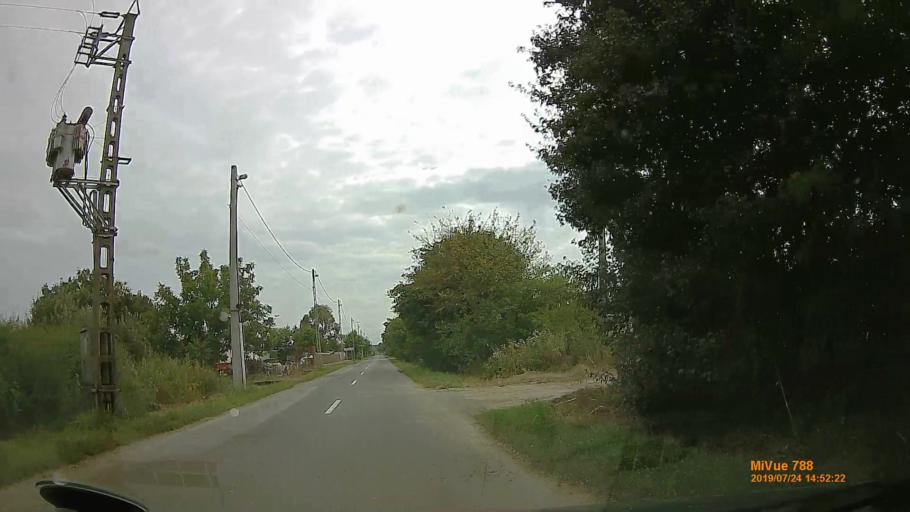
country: HU
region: Szabolcs-Szatmar-Bereg
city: Aranyosapati
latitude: 48.2634
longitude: 22.2886
